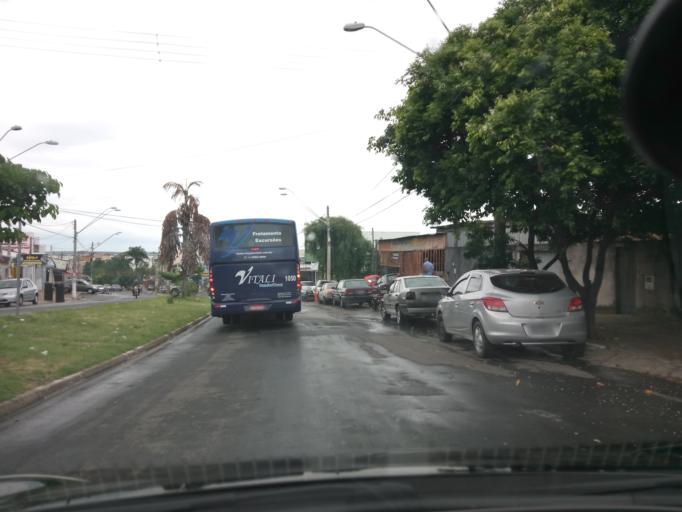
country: BR
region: Sao Paulo
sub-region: Campinas
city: Campinas
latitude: -22.9803
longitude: -47.1221
